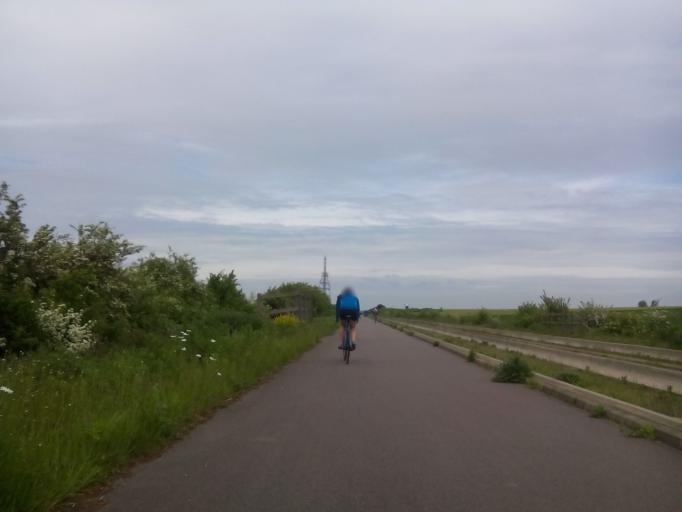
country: GB
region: England
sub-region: Cambridgeshire
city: Swavesey
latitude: 52.2964
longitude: 0.0373
